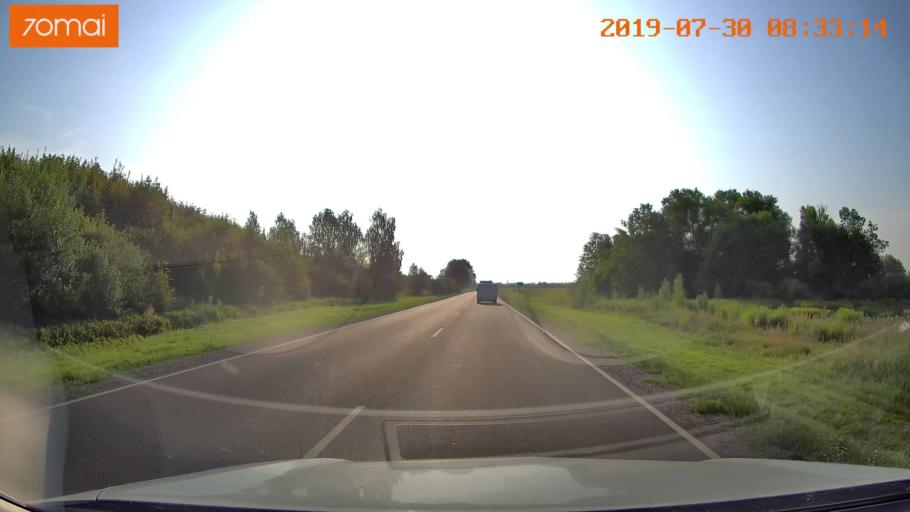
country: RU
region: Kaliningrad
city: Chernyakhovsk
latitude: 54.6363
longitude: 21.7425
